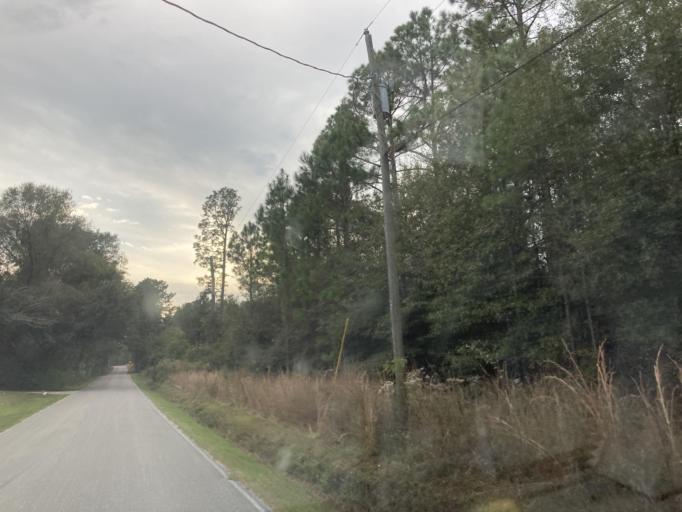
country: US
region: Mississippi
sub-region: Lamar County
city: Purvis
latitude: 31.1791
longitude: -89.3870
